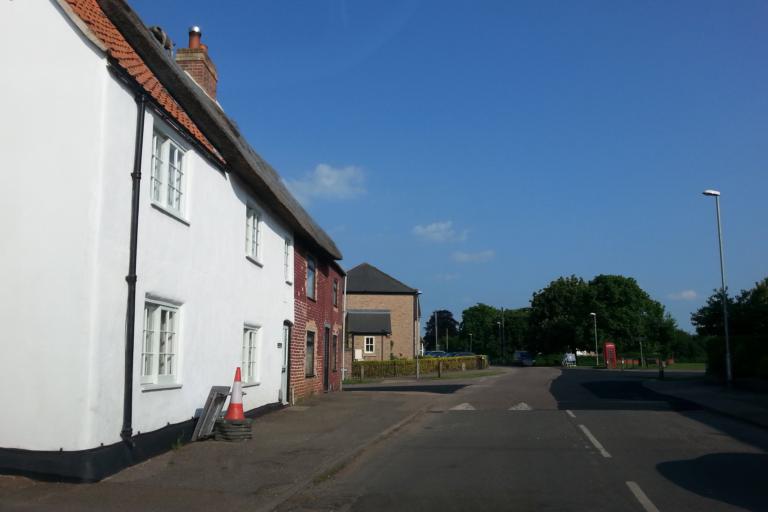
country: GB
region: England
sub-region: Cambridgeshire
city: Swavesey
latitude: 52.3162
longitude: 0.0188
